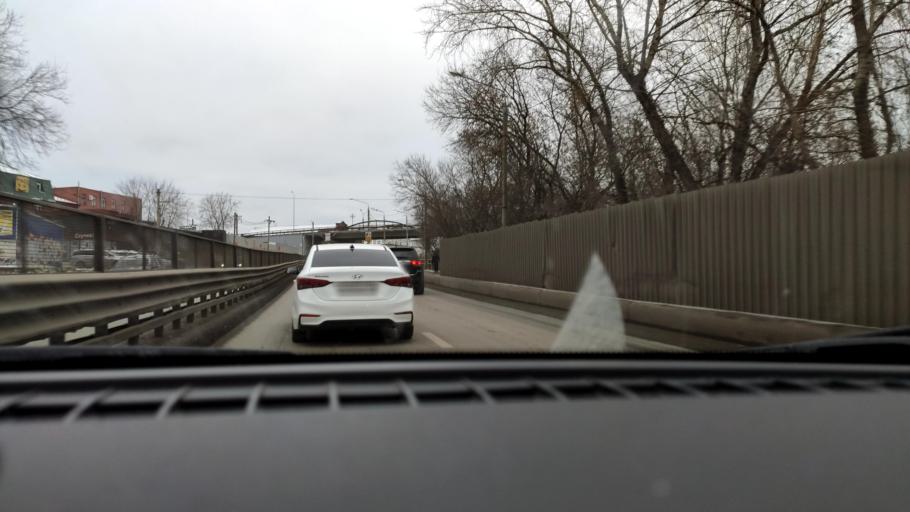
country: RU
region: Perm
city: Perm
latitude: 57.9988
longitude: 56.2255
